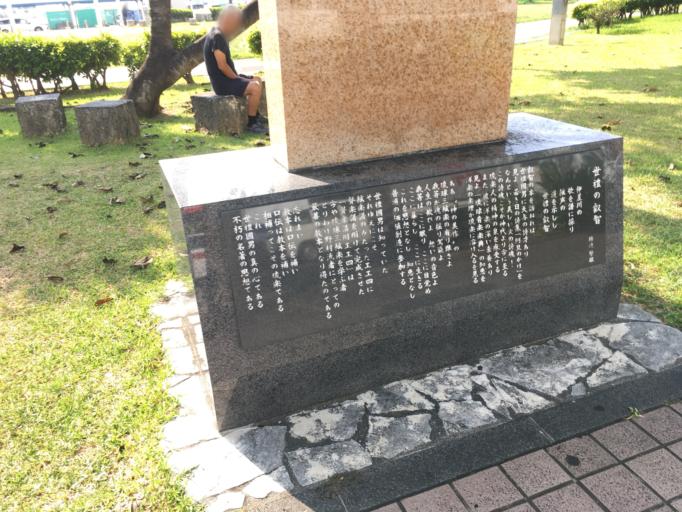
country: JP
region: Okinawa
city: Naha-shi
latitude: 26.2245
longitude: 127.6845
